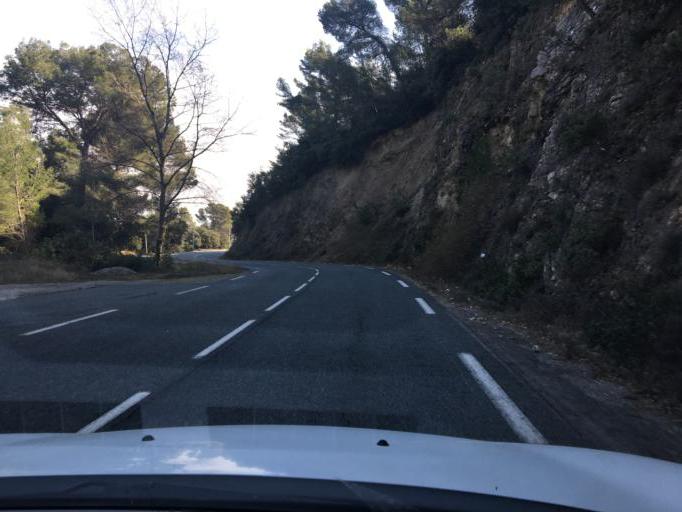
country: FR
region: Provence-Alpes-Cote d'Azur
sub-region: Departement du Var
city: Callas
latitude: 43.6025
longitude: 6.5499
